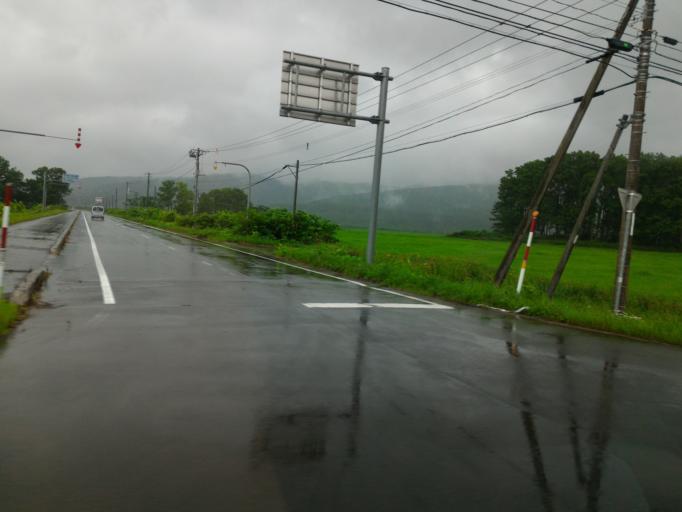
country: JP
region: Hokkaido
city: Makubetsu
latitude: 44.8709
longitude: 142.0408
